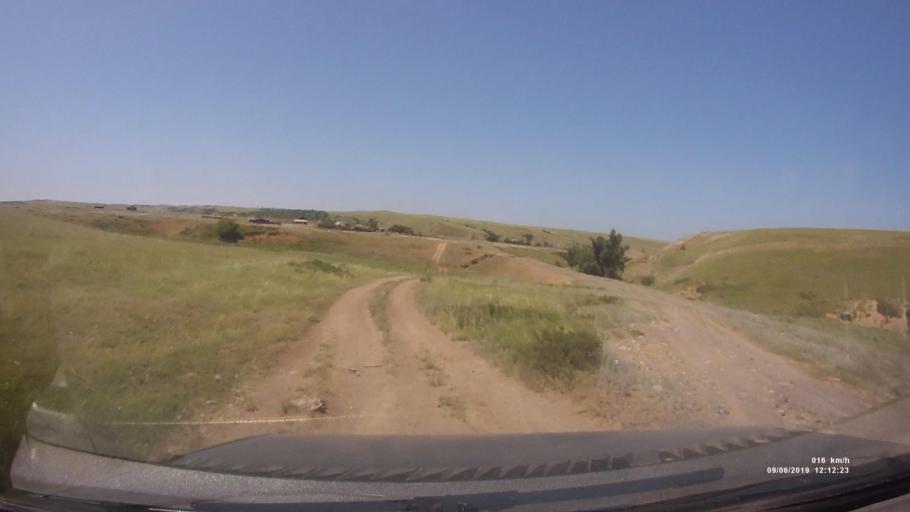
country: RU
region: Rostov
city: Staraya Stanitsa
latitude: 48.2505
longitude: 40.3289
